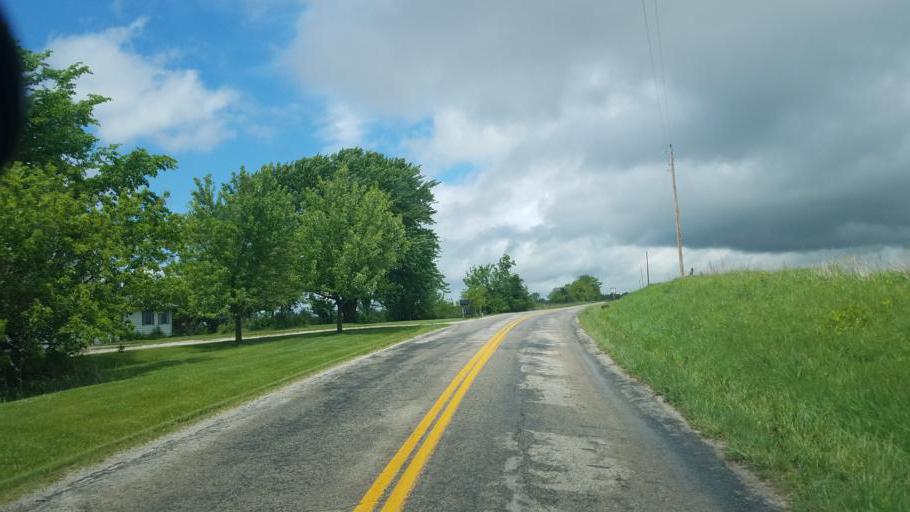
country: US
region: Iowa
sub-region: Decatur County
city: Leon
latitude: 40.5561
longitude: -93.7413
